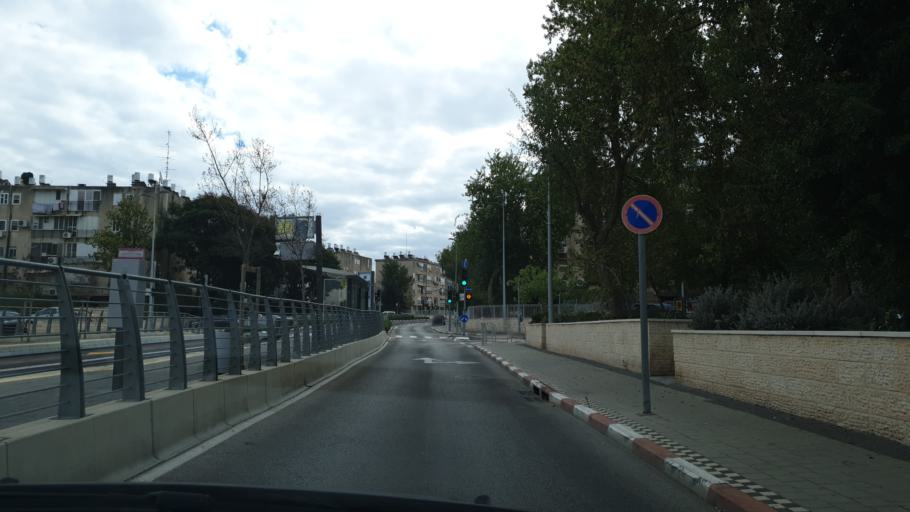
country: IL
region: Haifa
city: Qiryat Ata
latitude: 32.8181
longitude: 35.1127
